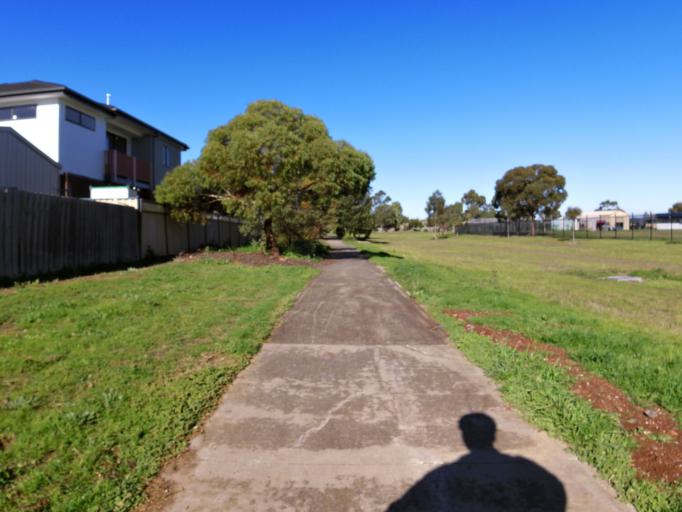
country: AU
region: Victoria
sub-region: Wyndham
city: Tarneit
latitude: -37.8668
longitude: 144.6780
